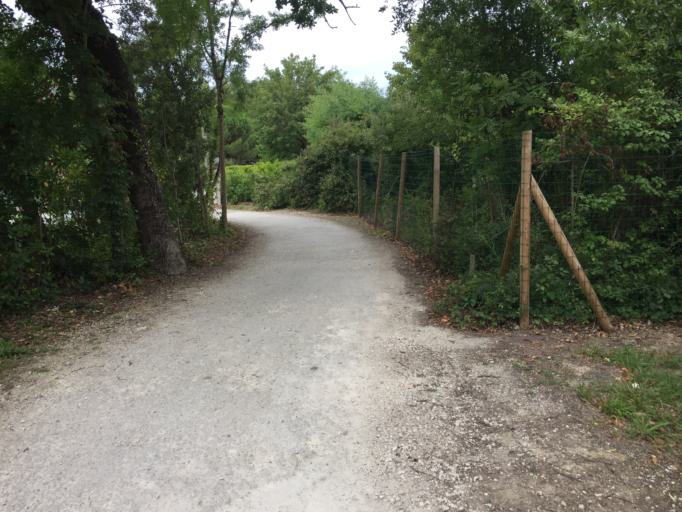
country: FR
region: Poitou-Charentes
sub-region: Departement de la Charente-Maritime
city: Boyard-Ville
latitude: 45.9801
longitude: -1.2944
